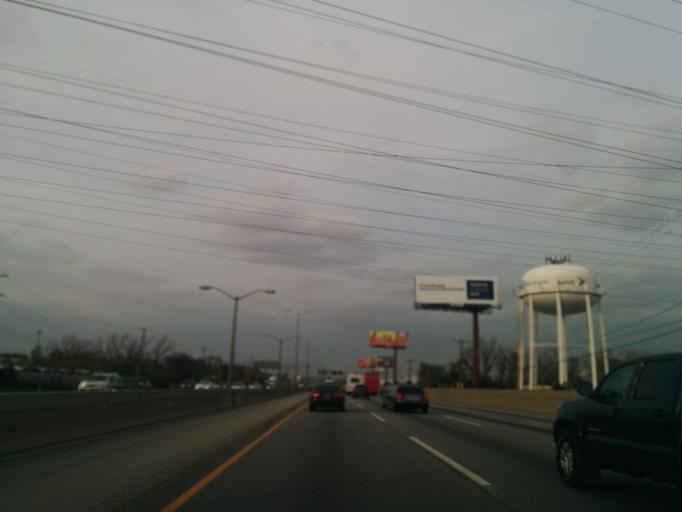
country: US
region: Illinois
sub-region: Cook County
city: Northlake
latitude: 41.9242
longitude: -87.9196
